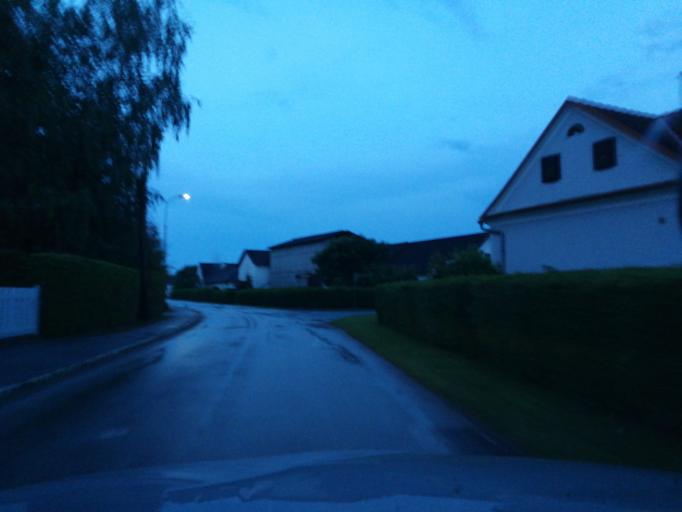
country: AT
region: Burgenland
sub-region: Politischer Bezirk Jennersdorf
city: Konigsdorf
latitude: 47.0050
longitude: 16.1664
